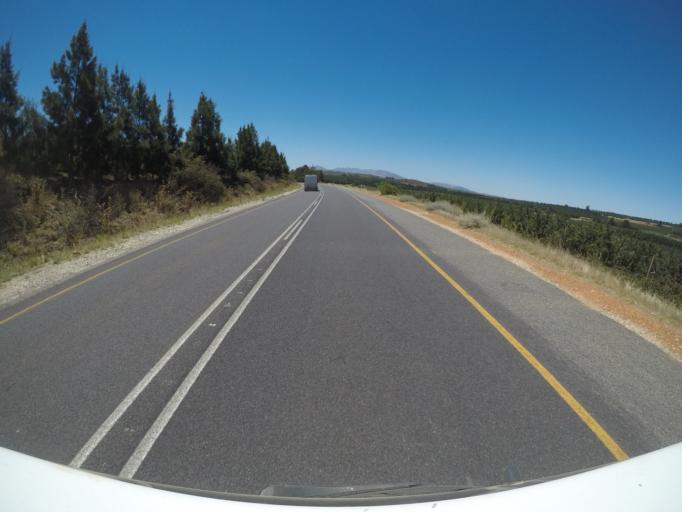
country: ZA
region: Western Cape
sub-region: Overberg District Municipality
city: Grabouw
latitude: -34.0576
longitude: 19.1430
